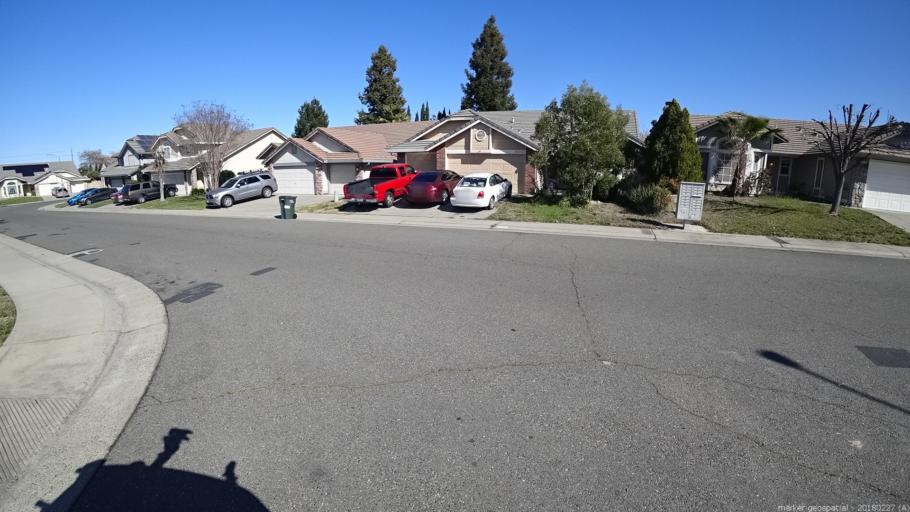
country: US
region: California
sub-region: Sacramento County
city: North Highlands
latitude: 38.7271
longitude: -121.3884
